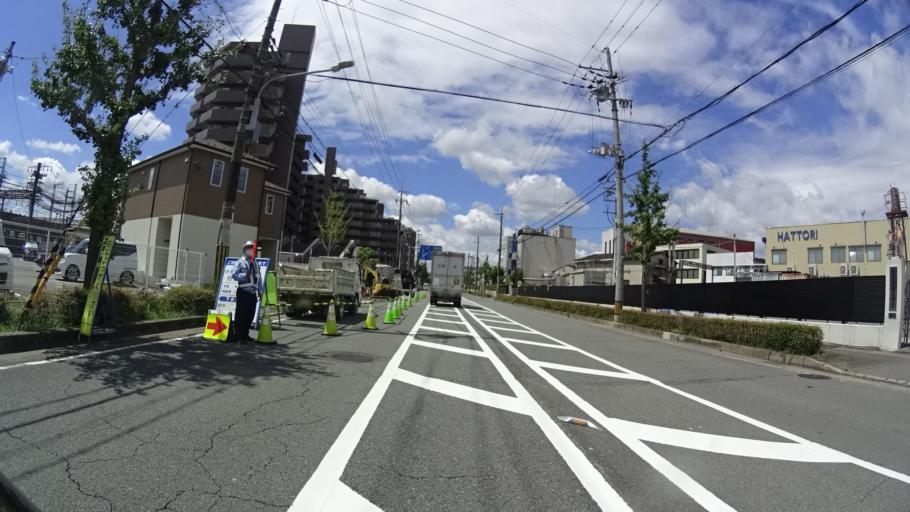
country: JP
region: Kyoto
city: Yawata
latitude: 34.8991
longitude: 135.7073
